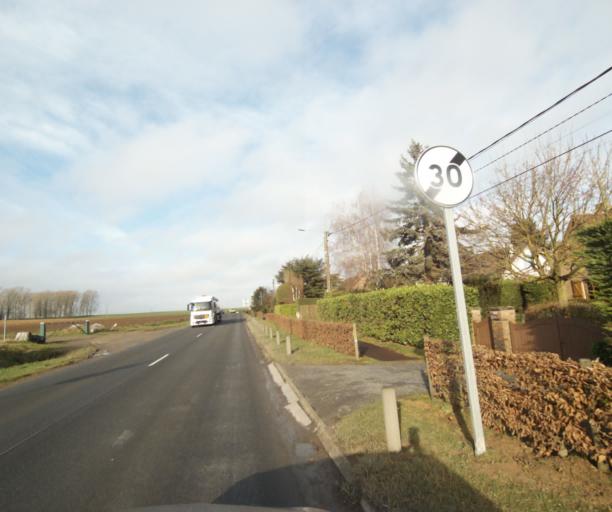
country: FR
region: Nord-Pas-de-Calais
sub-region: Departement du Nord
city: Thiant
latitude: 50.2832
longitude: 3.4511
